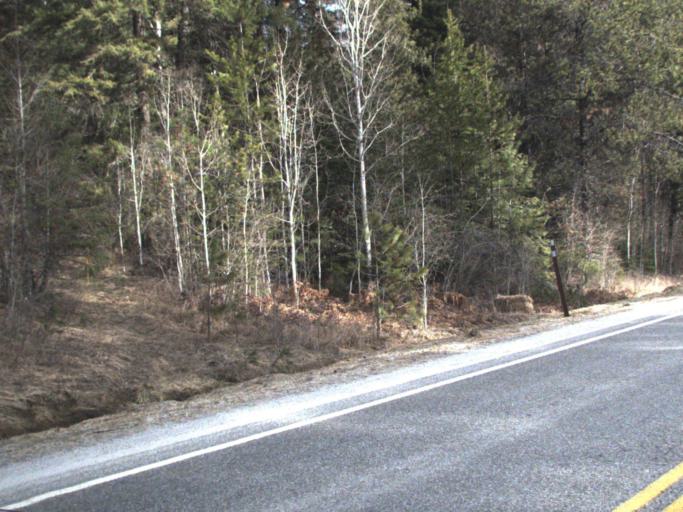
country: US
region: Washington
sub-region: Pend Oreille County
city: Newport
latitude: 48.4216
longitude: -117.3184
